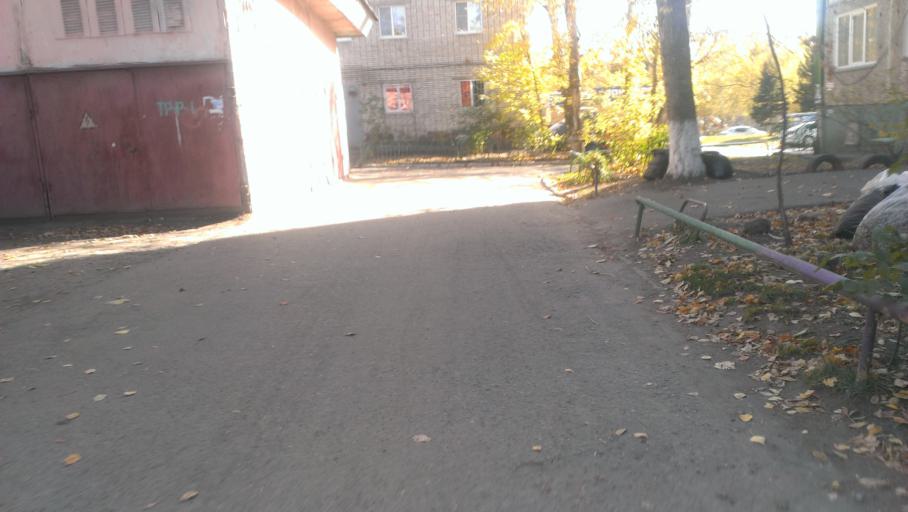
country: RU
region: Altai Krai
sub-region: Gorod Barnaulskiy
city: Barnaul
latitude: 53.3496
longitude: 83.6889
